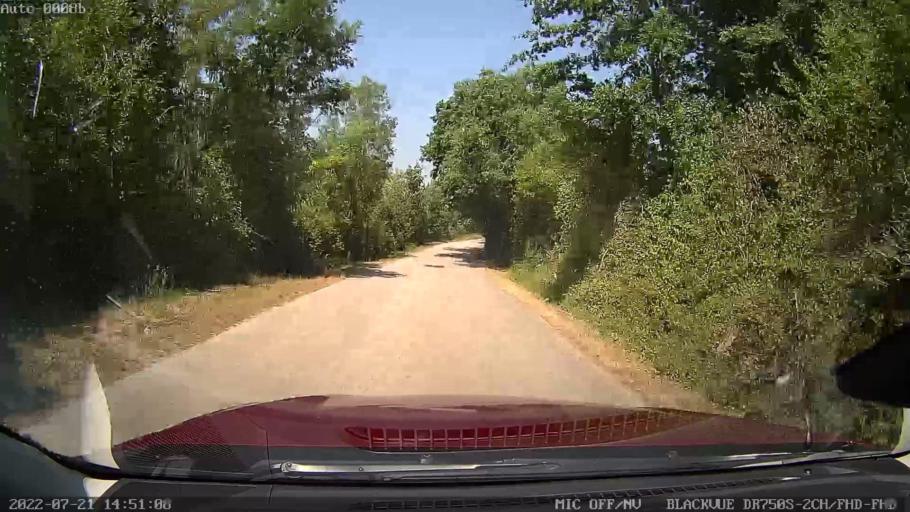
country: HR
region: Istarska
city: Pazin
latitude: 45.1665
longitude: 13.9197
